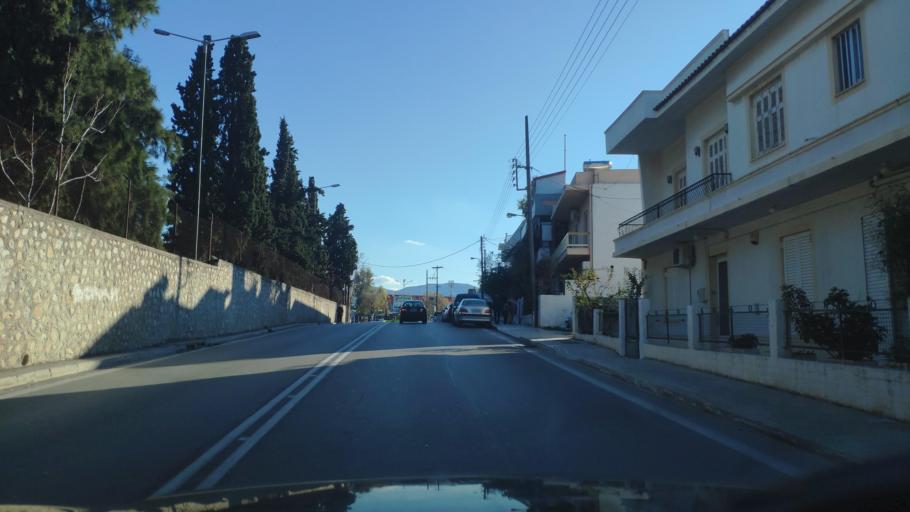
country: GR
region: Peloponnese
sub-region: Nomos Korinthias
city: Korinthos
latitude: 37.9313
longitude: 22.9284
